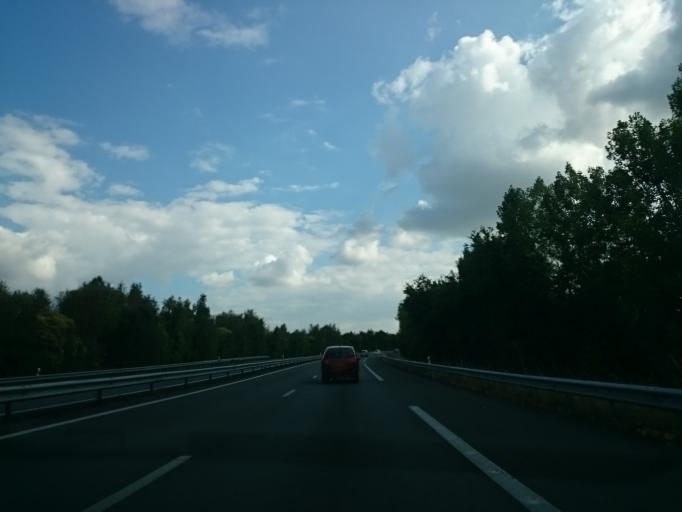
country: FR
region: Brittany
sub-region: Departement d'Ille-et-Vilaine
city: Crevin
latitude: 47.9342
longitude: -1.6732
